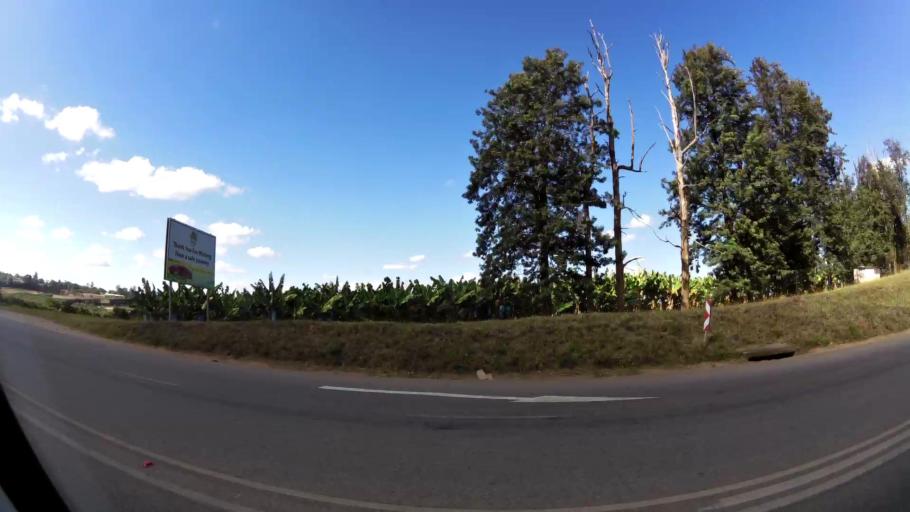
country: ZA
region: Limpopo
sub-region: Mopani District Municipality
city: Tzaneen
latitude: -23.8145
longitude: 30.1732
